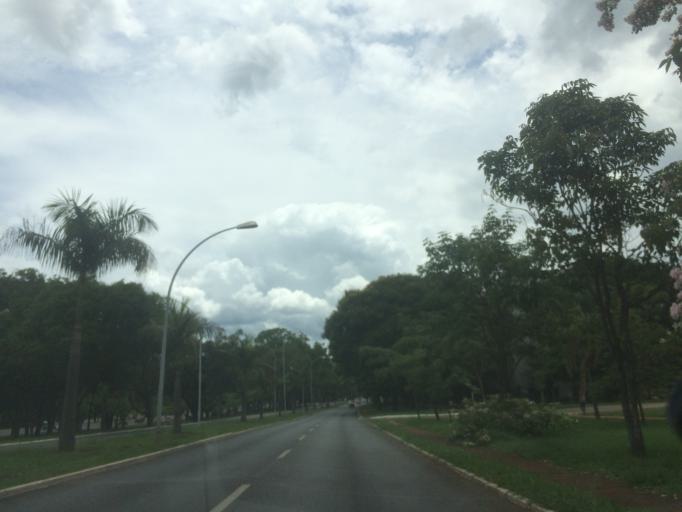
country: BR
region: Federal District
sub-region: Brasilia
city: Brasilia
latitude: -15.7800
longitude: -47.8814
